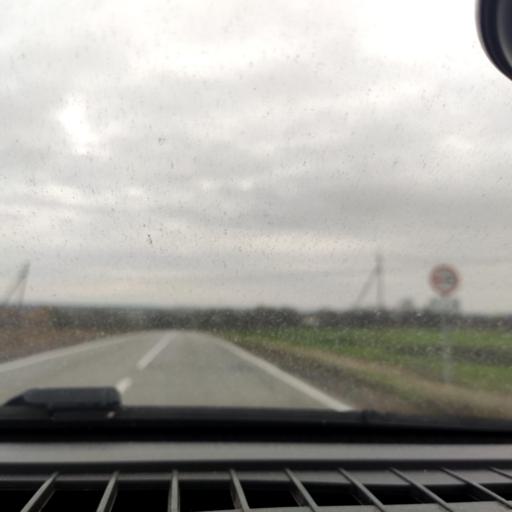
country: RU
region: Voronezj
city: Ostrogozhsk
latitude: 50.7901
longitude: 38.9412
